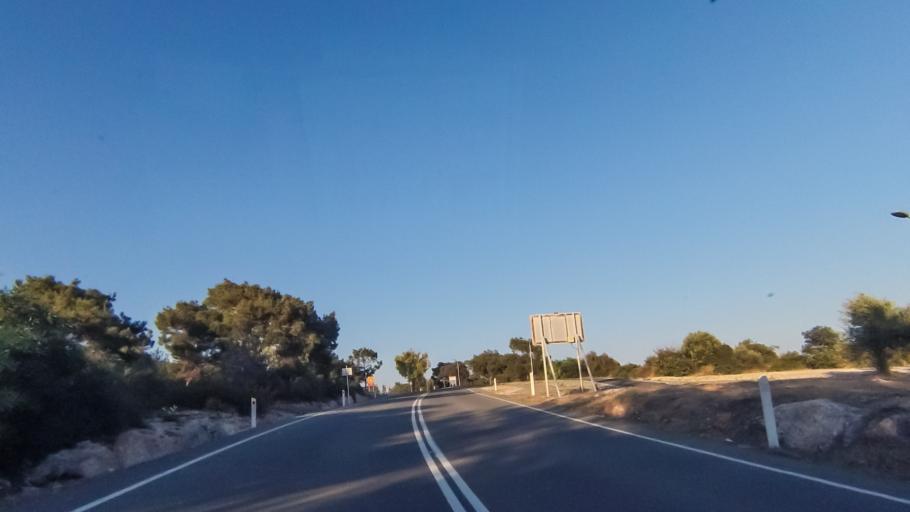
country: CY
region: Limassol
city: Sotira
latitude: 34.6726
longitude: 32.8295
